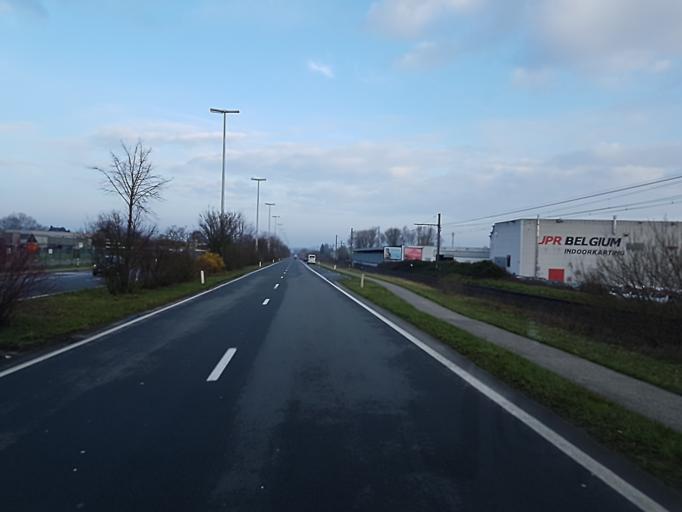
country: BE
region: Flanders
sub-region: Provincie Oost-Vlaanderen
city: Sint-Niklaas
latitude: 51.1659
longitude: 4.1665
